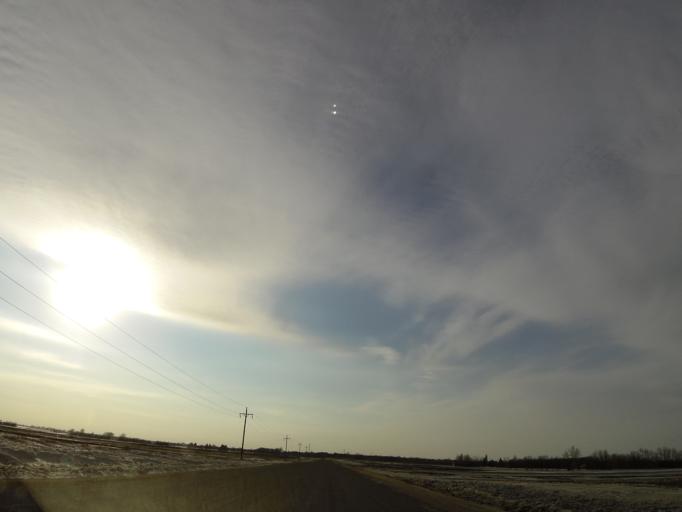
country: US
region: North Dakota
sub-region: Walsh County
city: Grafton
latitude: 48.4197
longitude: -97.3665
